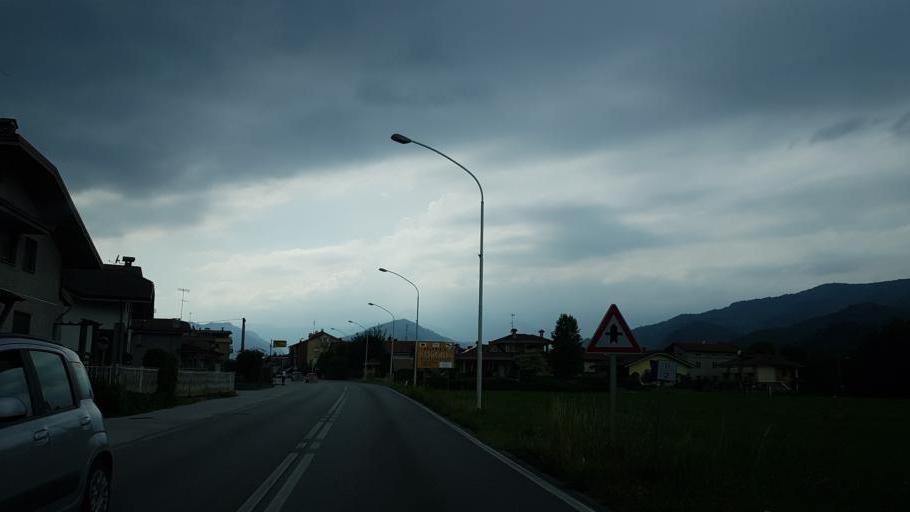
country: IT
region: Piedmont
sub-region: Provincia di Cuneo
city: Roccasparvera
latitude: 44.3346
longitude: 7.4620
